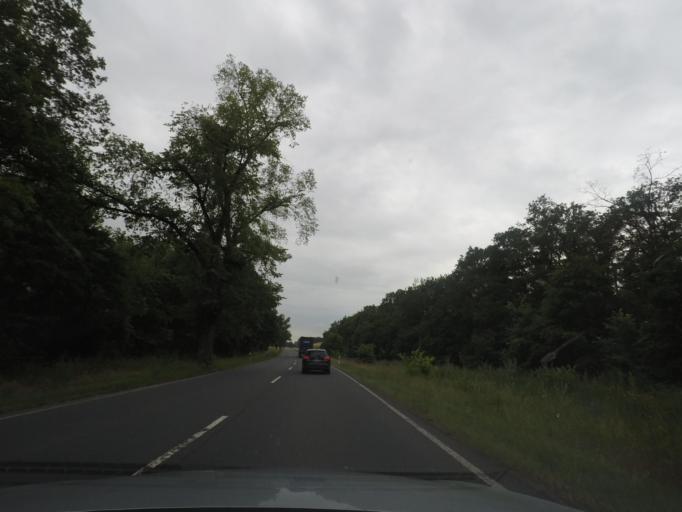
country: DE
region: Saxony-Anhalt
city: Haldensleben I
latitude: 52.3169
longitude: 11.4305
